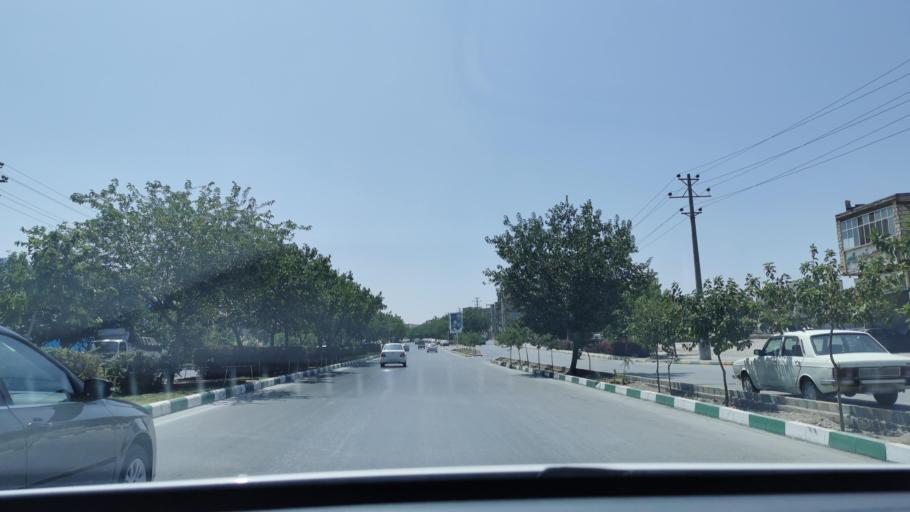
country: IR
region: Razavi Khorasan
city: Mashhad
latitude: 36.3492
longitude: 59.6285
